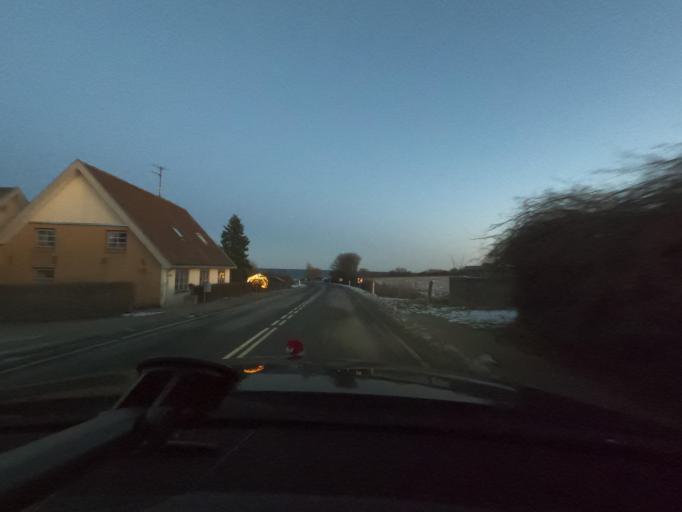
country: DE
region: Schleswig-Holstein
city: Pommerby
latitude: 54.8551
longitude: 9.9874
